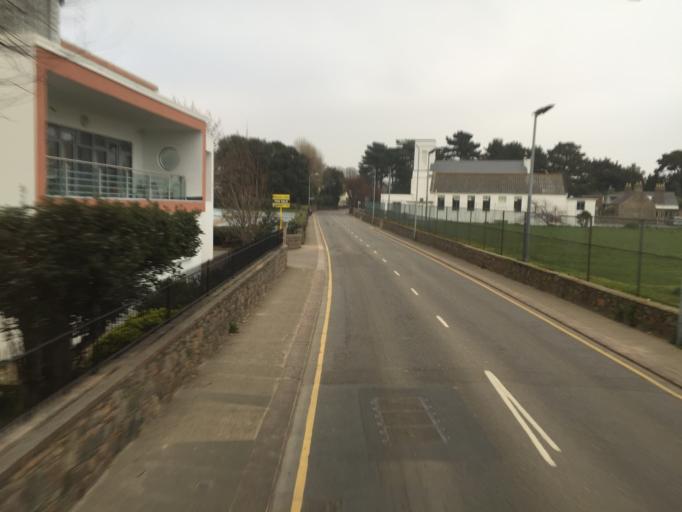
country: JE
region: St Helier
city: Saint Helier
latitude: 49.1983
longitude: -2.1443
